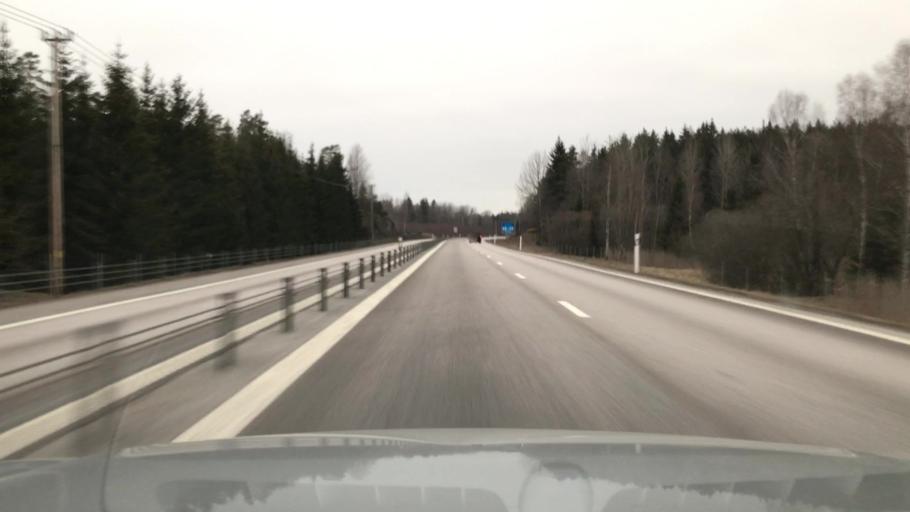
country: SE
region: OEstergoetland
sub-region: Valdemarsviks Kommun
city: Gusum
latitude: 58.2651
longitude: 16.5212
